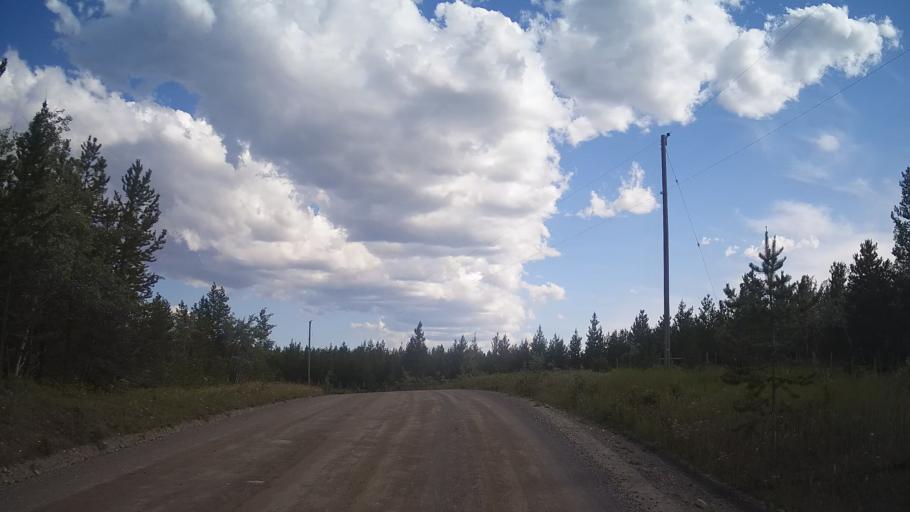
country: CA
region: British Columbia
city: Cache Creek
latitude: 51.2731
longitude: -121.7280
